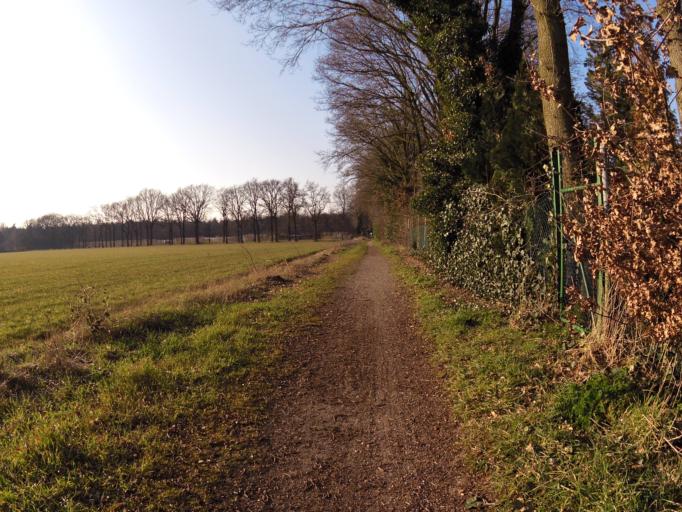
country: NL
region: North Brabant
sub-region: Gemeente Maasdonk
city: Geffen
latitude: 51.7034
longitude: 5.4249
